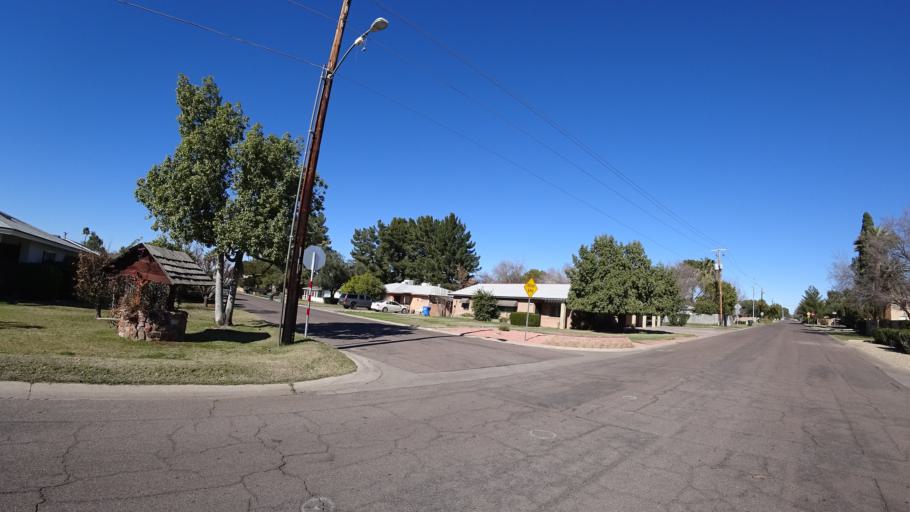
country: US
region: Arizona
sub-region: Maricopa County
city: Phoenix
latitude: 33.5118
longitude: -112.0607
